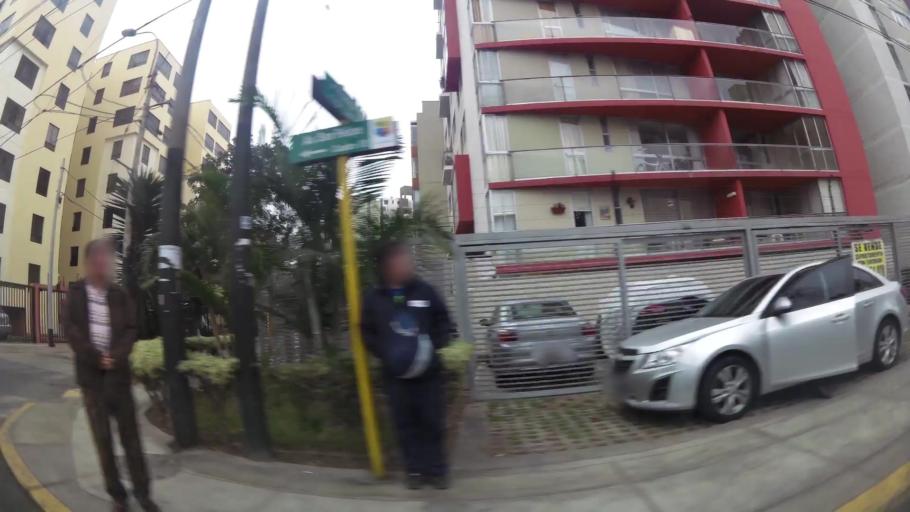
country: PE
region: Lima
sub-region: Lima
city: San Isidro
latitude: -12.0835
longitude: -77.0533
